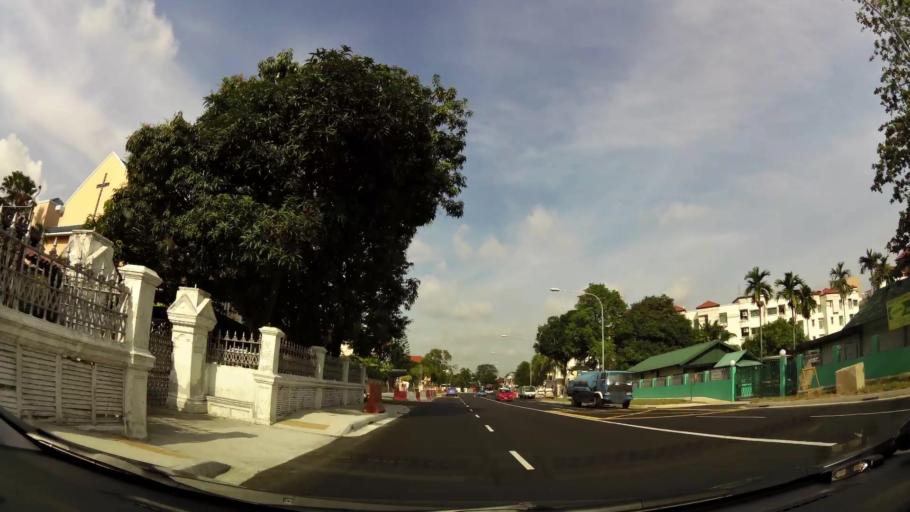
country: SG
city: Singapore
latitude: 1.2898
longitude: 103.7753
